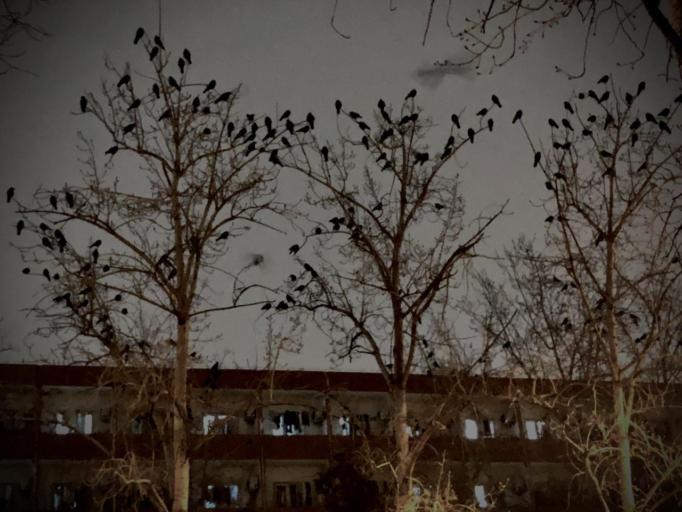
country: CN
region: Beijing
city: Jinrongjie
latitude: 39.9566
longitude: 116.3563
